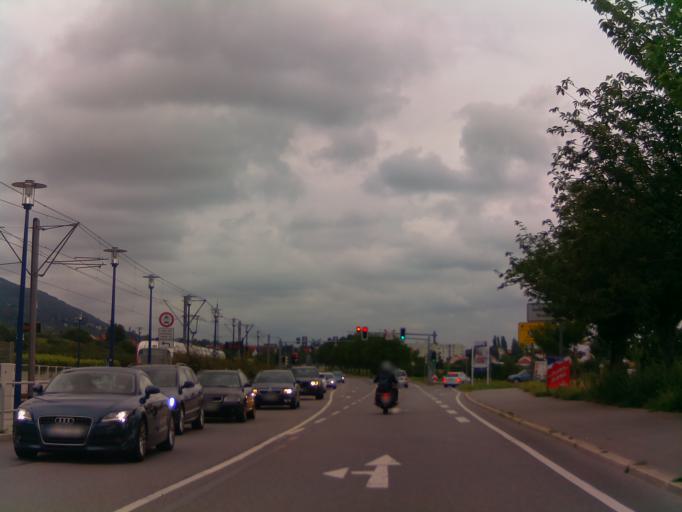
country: DE
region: Baden-Wuerttemberg
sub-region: Karlsruhe Region
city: Schriesheim
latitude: 49.5097
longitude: 8.6558
